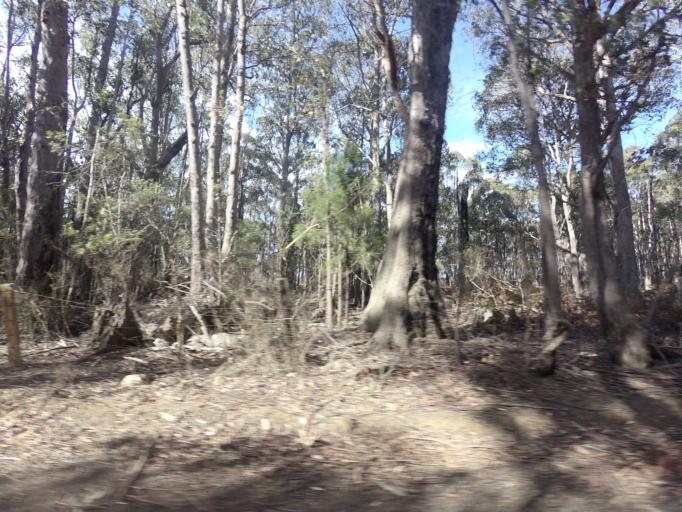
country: AU
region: Tasmania
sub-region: Sorell
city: Sorell
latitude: -42.4924
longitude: 147.4810
